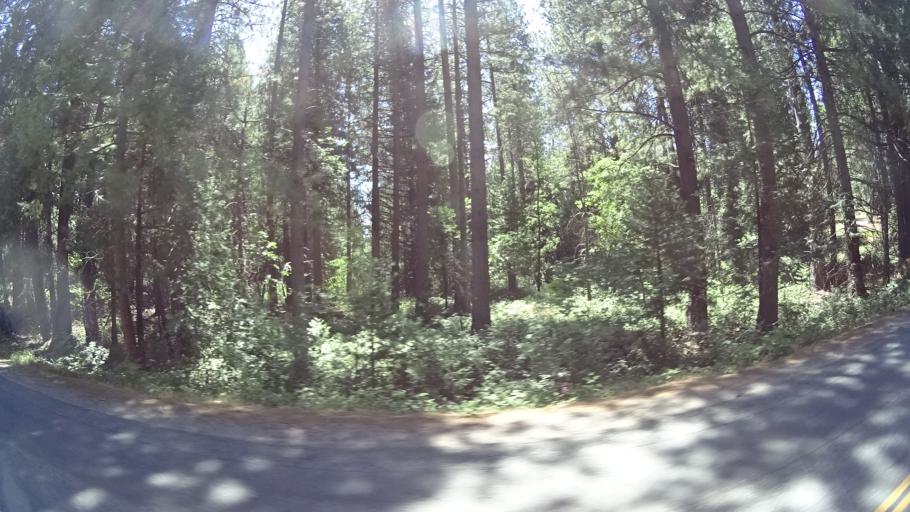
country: US
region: California
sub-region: Amador County
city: Pioneer
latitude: 38.4030
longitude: -120.5238
